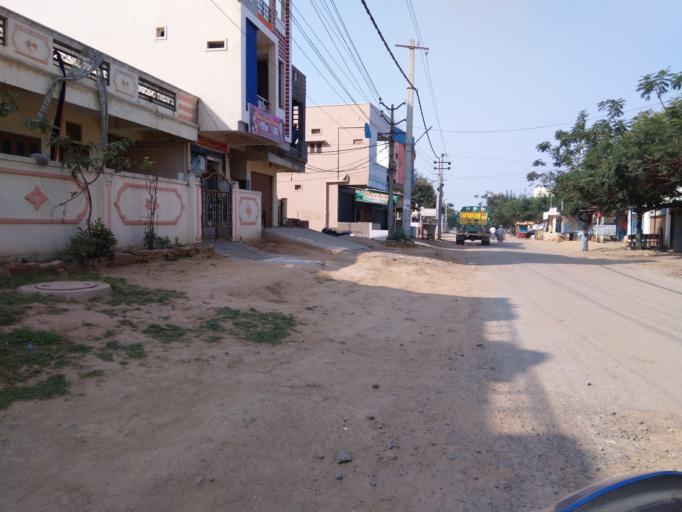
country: IN
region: Telangana
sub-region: Rangareddi
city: Quthbullapur
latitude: 17.5908
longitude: 78.4182
